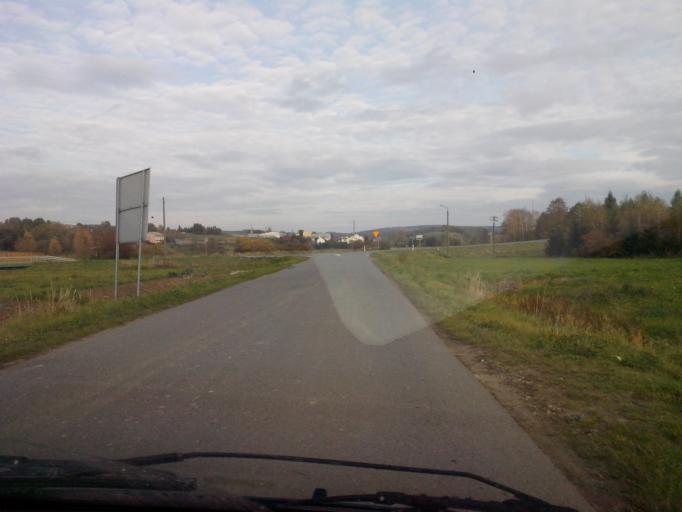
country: PL
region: Subcarpathian Voivodeship
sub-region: Powiat ropczycko-sedziszowski
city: Wielopole Skrzynskie
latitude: 49.9468
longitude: 21.6114
